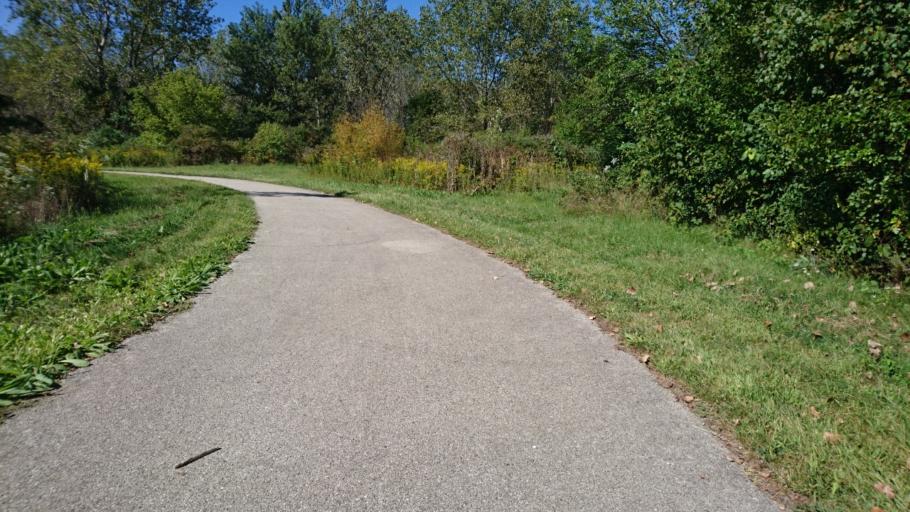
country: US
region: Illinois
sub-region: Cook County
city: Lansing
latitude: 41.5814
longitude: -87.5510
